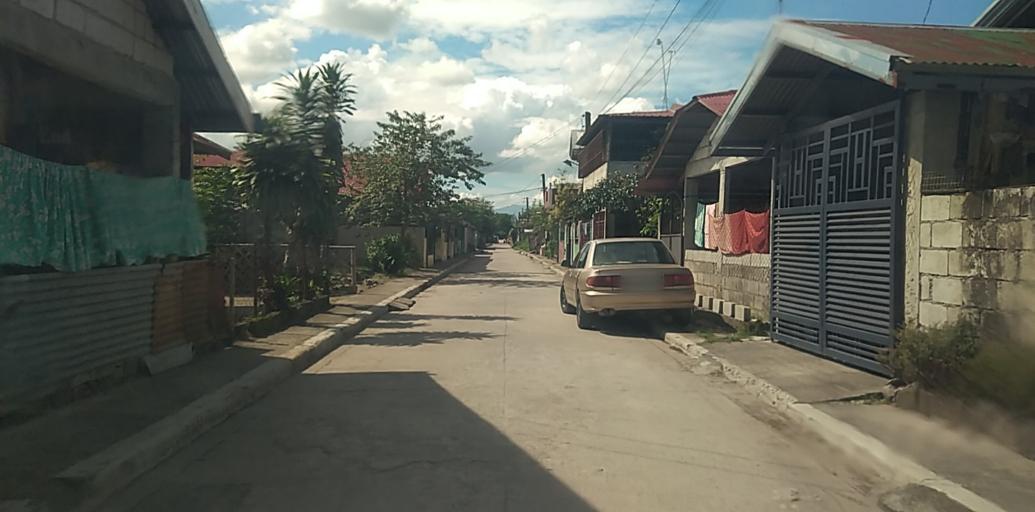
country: PH
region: Central Luzon
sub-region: Province of Pampanga
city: Buensuseso
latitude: 15.1921
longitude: 120.6634
